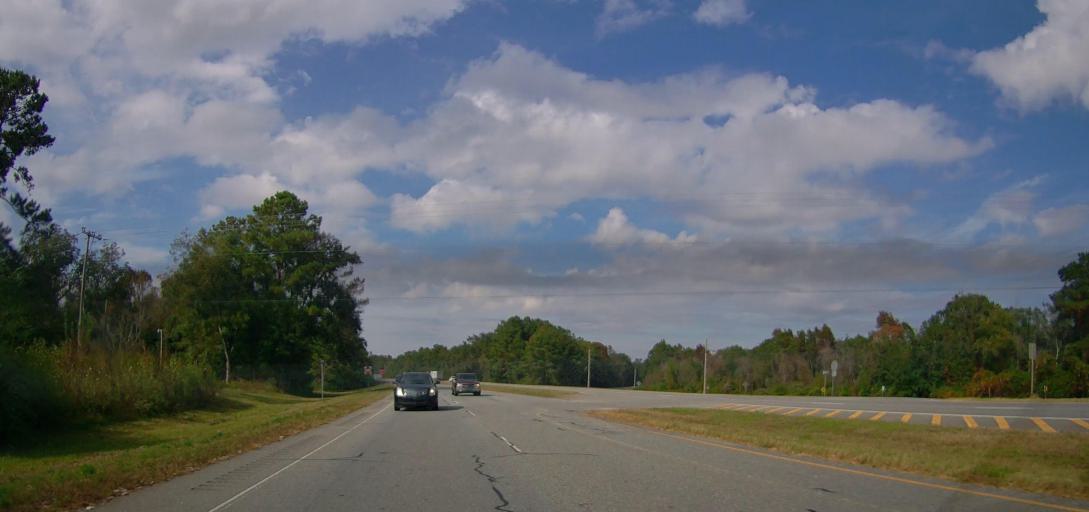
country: US
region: Georgia
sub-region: Mitchell County
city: Pelham
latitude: 31.1732
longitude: -84.1476
